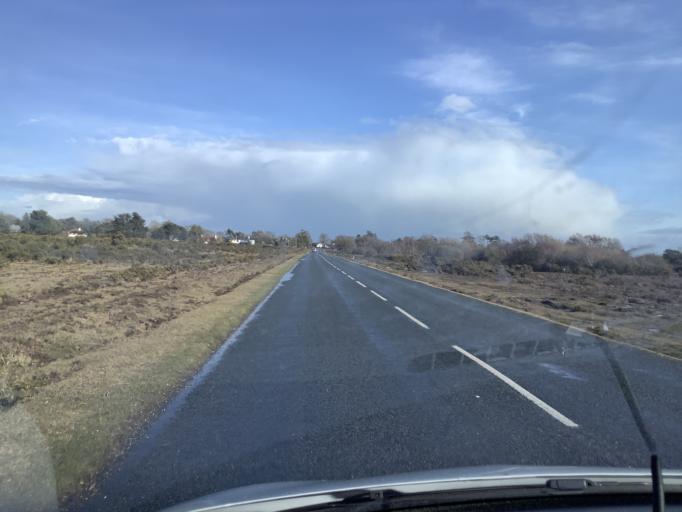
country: GB
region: England
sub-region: Hampshire
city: Marchwood
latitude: 50.8145
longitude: -1.4835
